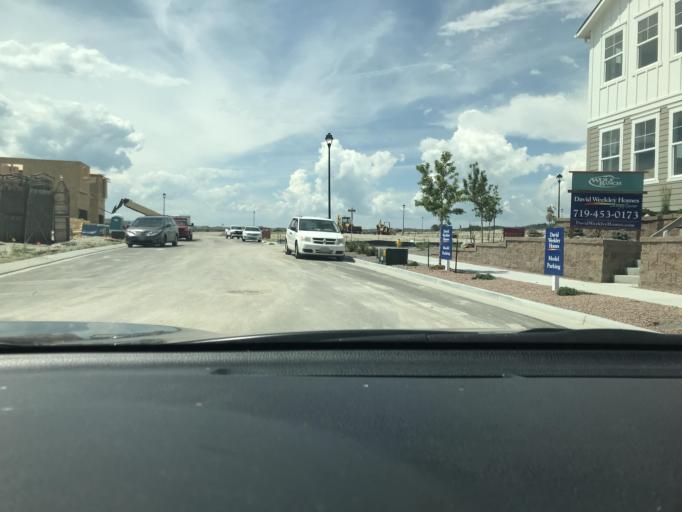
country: US
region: Colorado
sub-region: El Paso County
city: Black Forest
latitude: 38.9608
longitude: -104.7074
